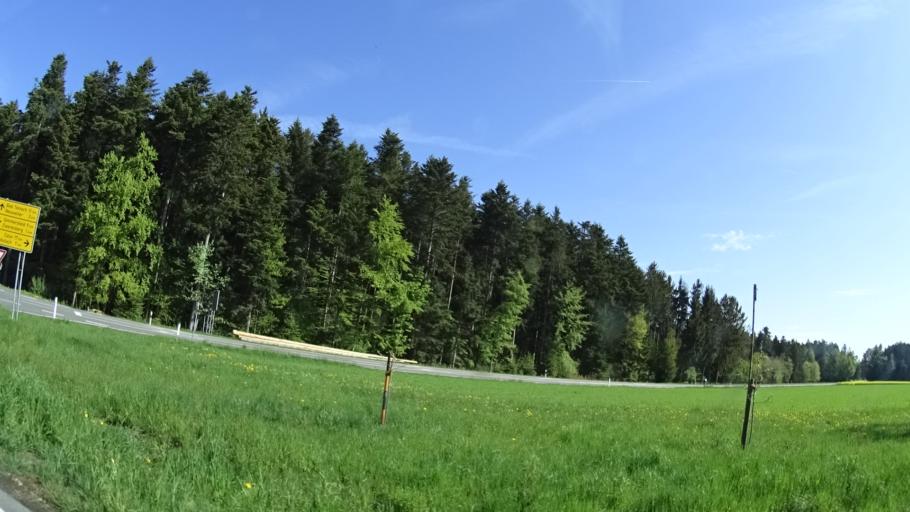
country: DE
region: Baden-Wuerttemberg
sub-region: Karlsruhe Region
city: Neuweiler
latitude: 48.6370
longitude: 8.6066
